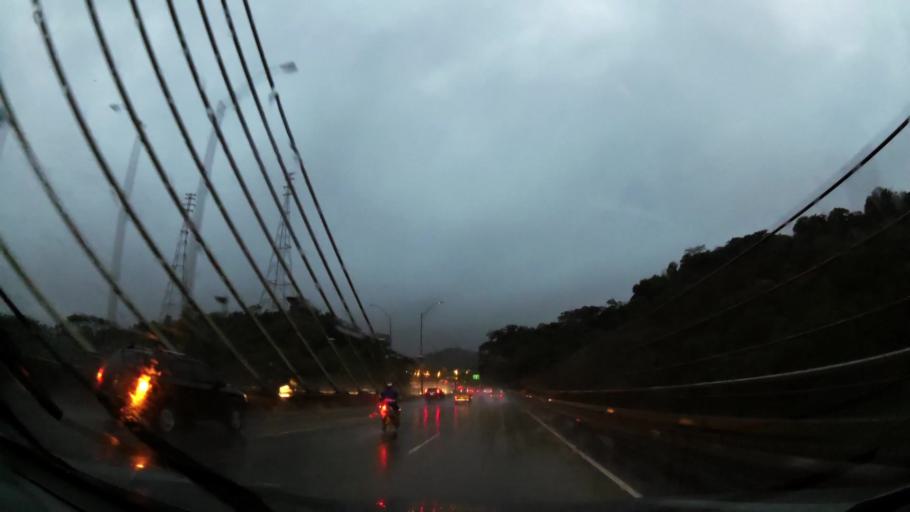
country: PA
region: Panama
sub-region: Distrito de Panama
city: Paraiso
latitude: 9.0290
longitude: -79.6372
